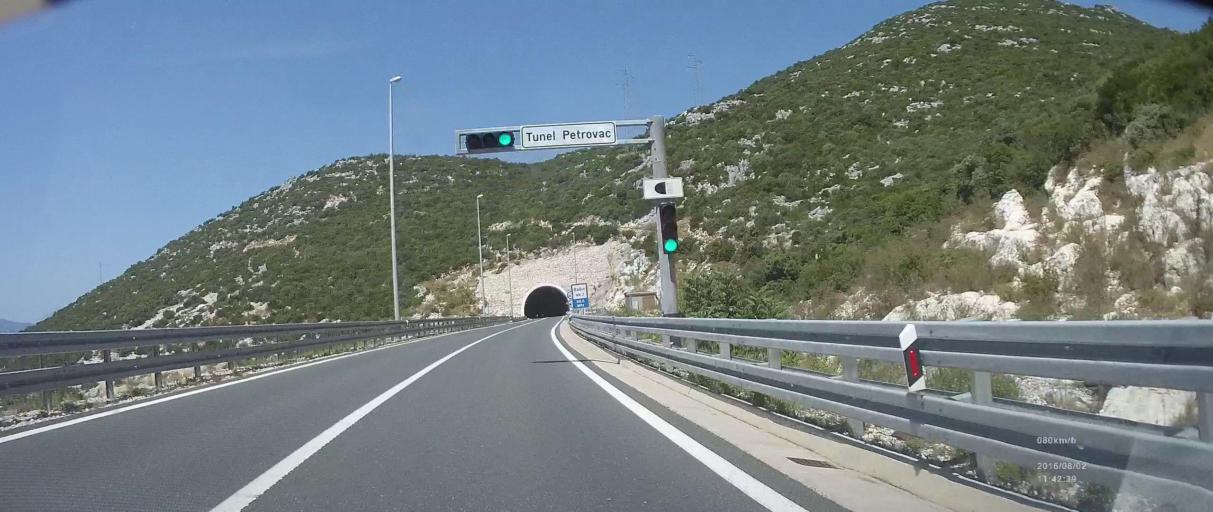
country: HR
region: Dubrovacko-Neretvanska
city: Komin
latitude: 43.0531
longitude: 17.4839
